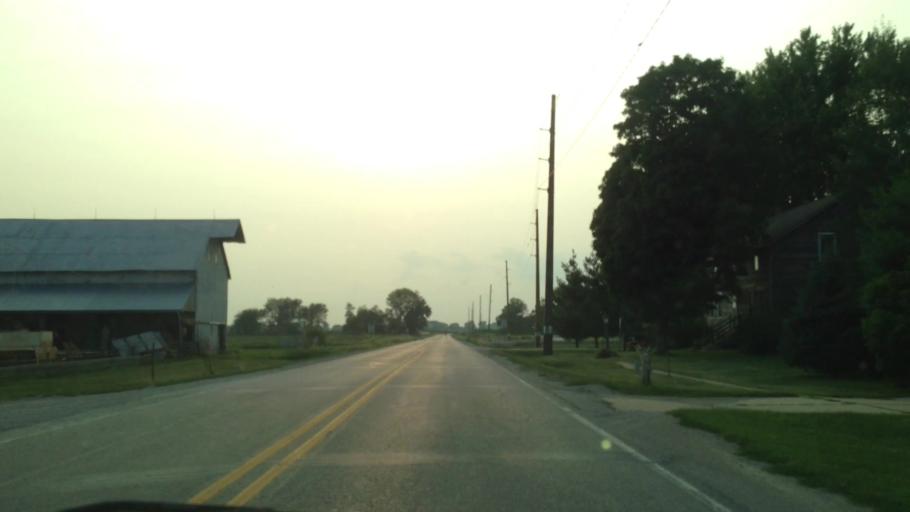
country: US
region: Iowa
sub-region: Iowa County
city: Marengo
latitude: 41.8023
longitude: -91.9418
